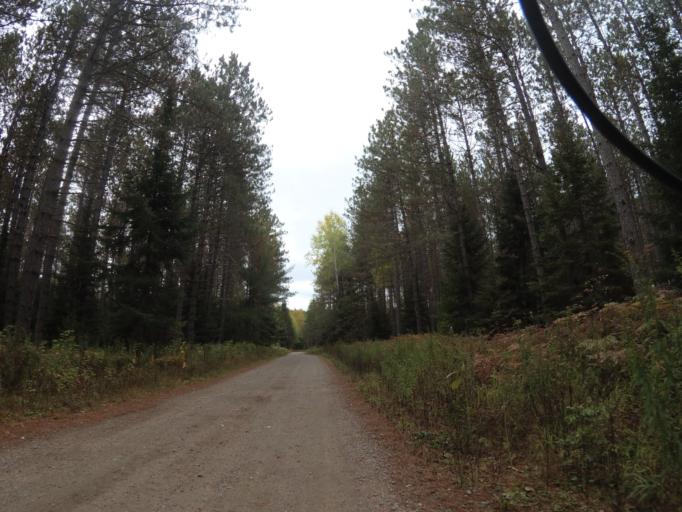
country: CA
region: Ontario
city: Pembroke
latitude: 45.2877
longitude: -77.2456
